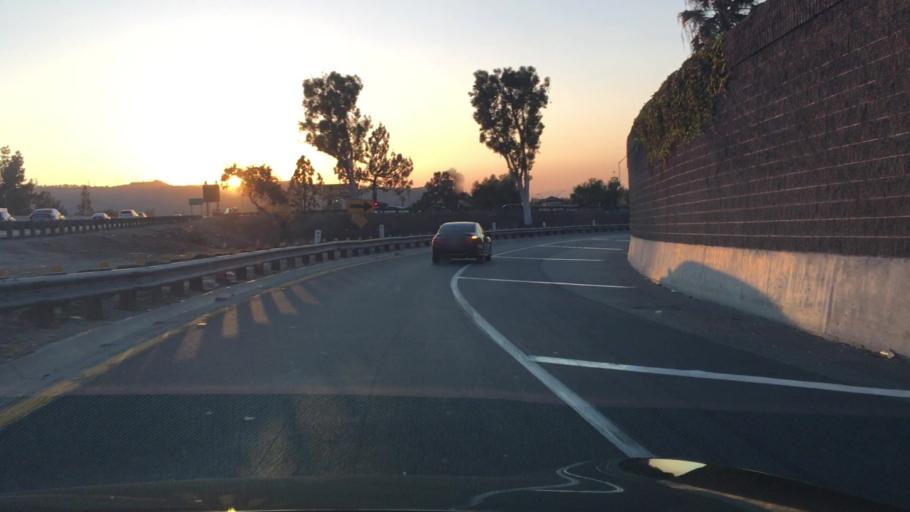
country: US
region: California
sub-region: Los Angeles County
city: Hacienda Heights
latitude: 34.0065
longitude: -117.9621
